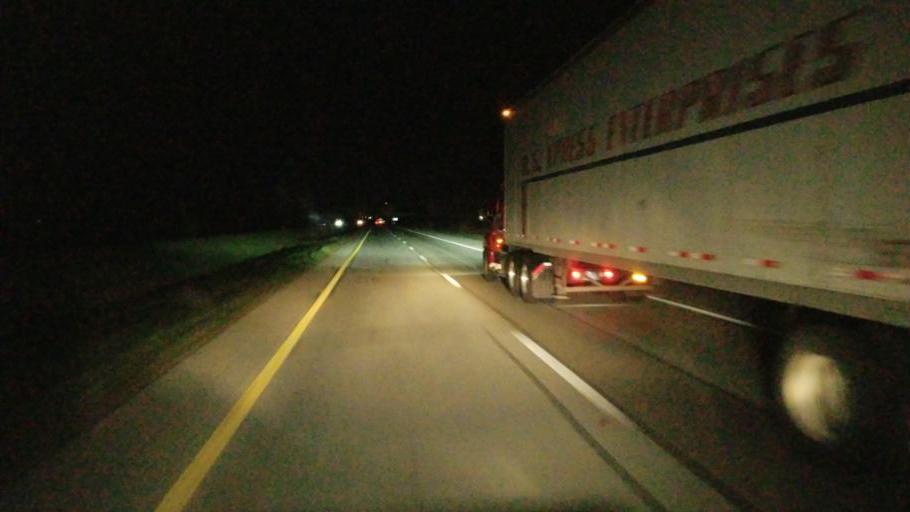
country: US
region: Ohio
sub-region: Preble County
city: Lewisburg
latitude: 39.8379
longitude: -84.4972
